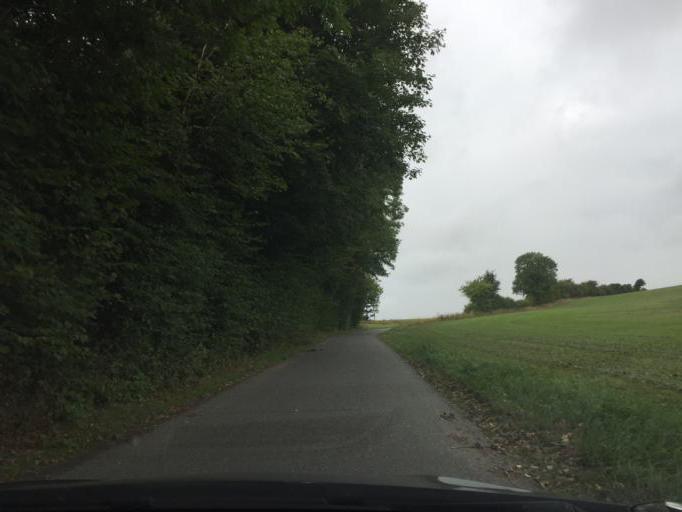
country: DK
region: South Denmark
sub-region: Assens Kommune
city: Harby
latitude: 55.1988
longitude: 10.0341
